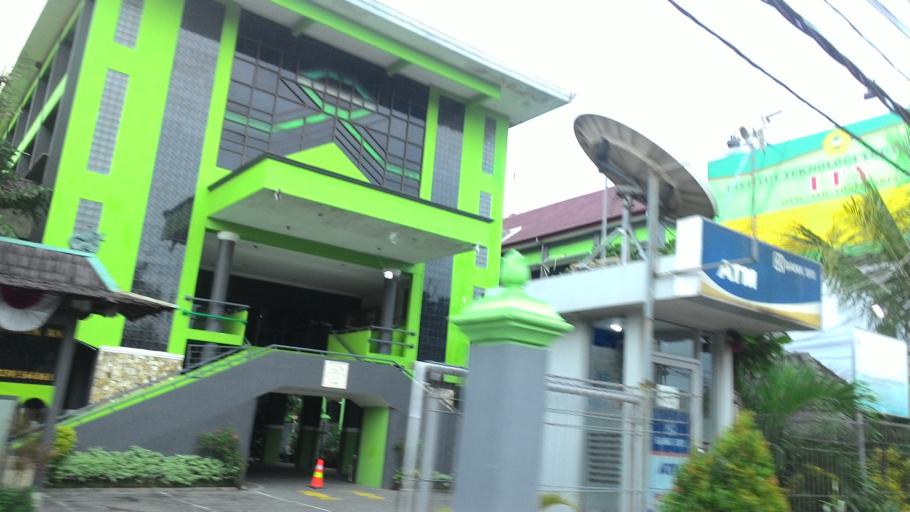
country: ID
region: Daerah Istimewa Yogyakarta
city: Yogyakarta
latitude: -7.7997
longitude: 110.4023
